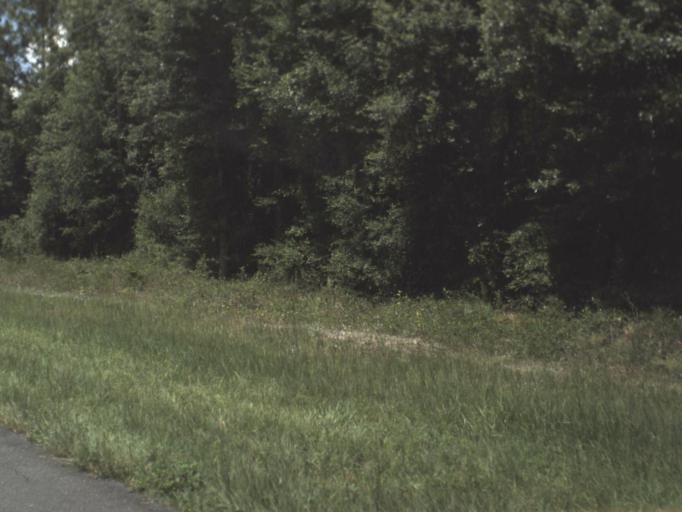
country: US
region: Florida
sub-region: Alachua County
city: Hawthorne
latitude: 29.6142
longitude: -82.0262
